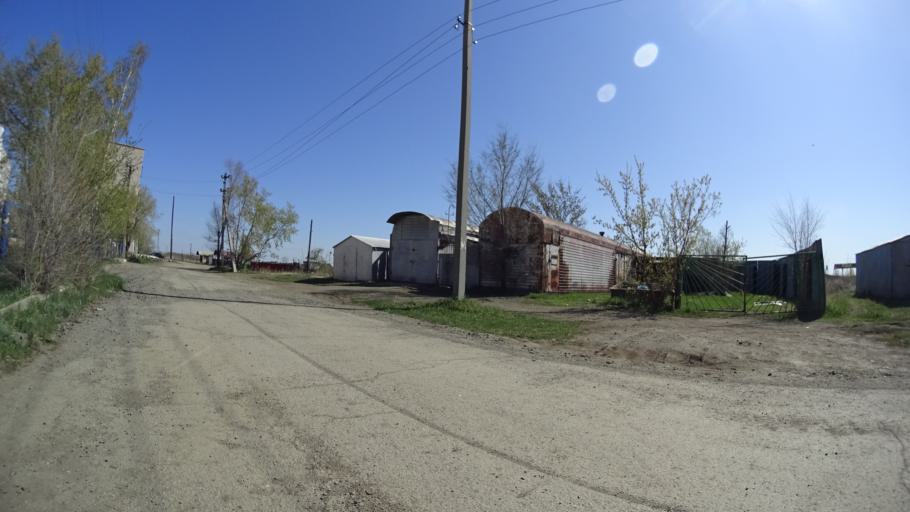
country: RU
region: Chelyabinsk
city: Troitsk
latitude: 54.1401
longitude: 61.5674
